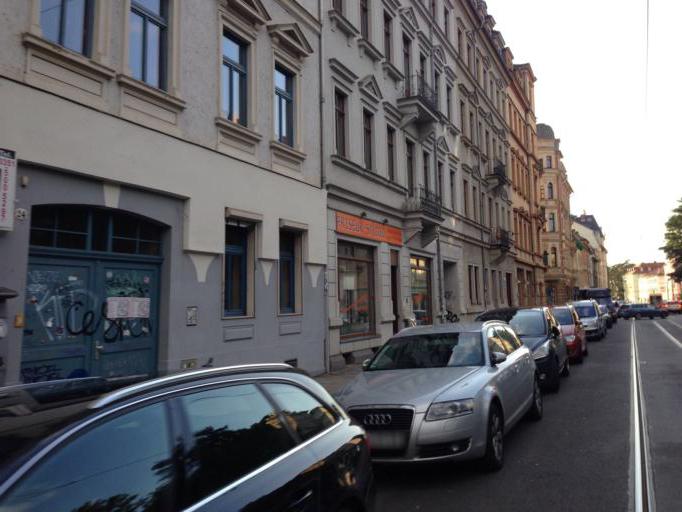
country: DE
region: Saxony
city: Albertstadt
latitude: 51.0706
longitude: 13.7531
